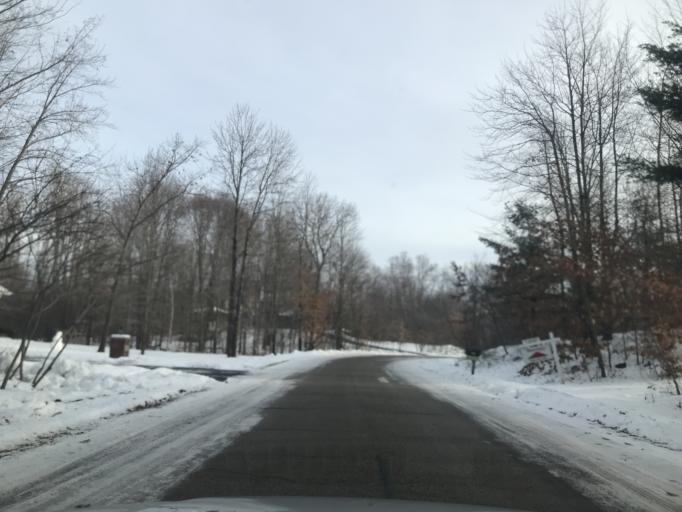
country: US
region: Wisconsin
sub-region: Brown County
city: Suamico
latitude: 44.6889
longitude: -88.0549
